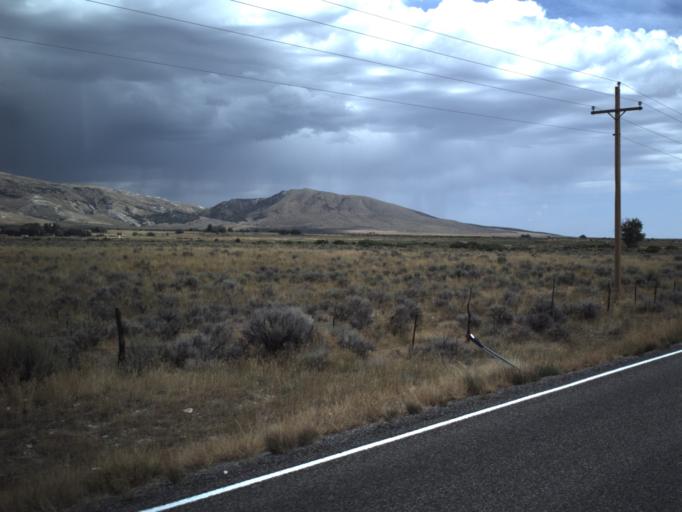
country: US
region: Idaho
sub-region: Cassia County
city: Burley
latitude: 41.8167
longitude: -113.3516
